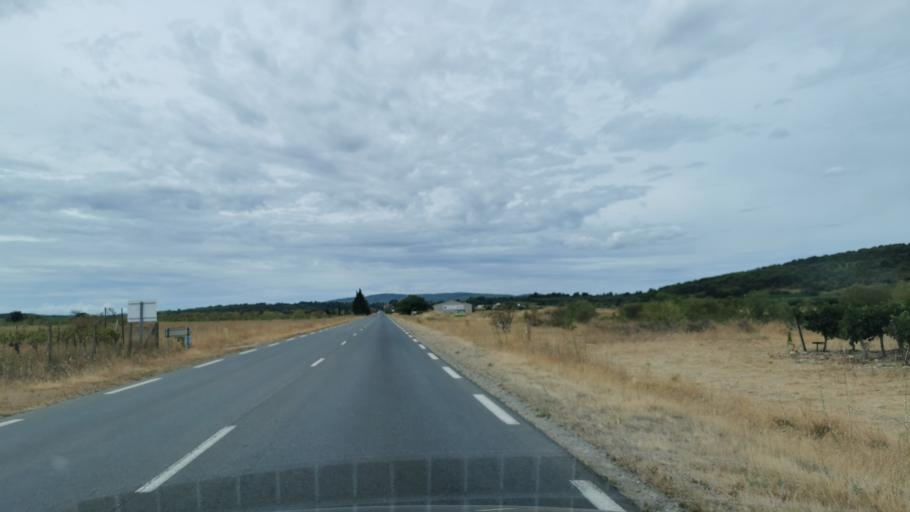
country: FR
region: Languedoc-Roussillon
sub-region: Departement de l'Aude
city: Argeliers
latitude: 43.3025
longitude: 2.8922
